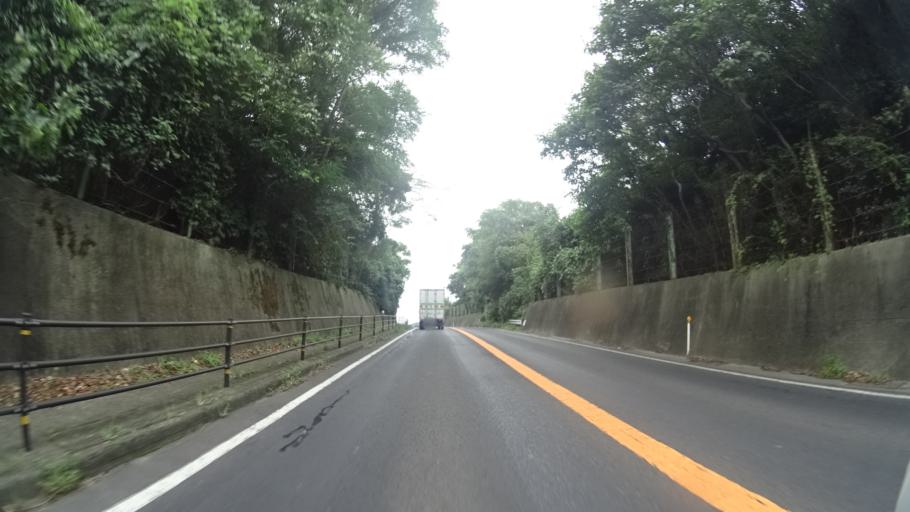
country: JP
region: Shimane
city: Odacho-oda
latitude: 35.1895
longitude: 132.4319
